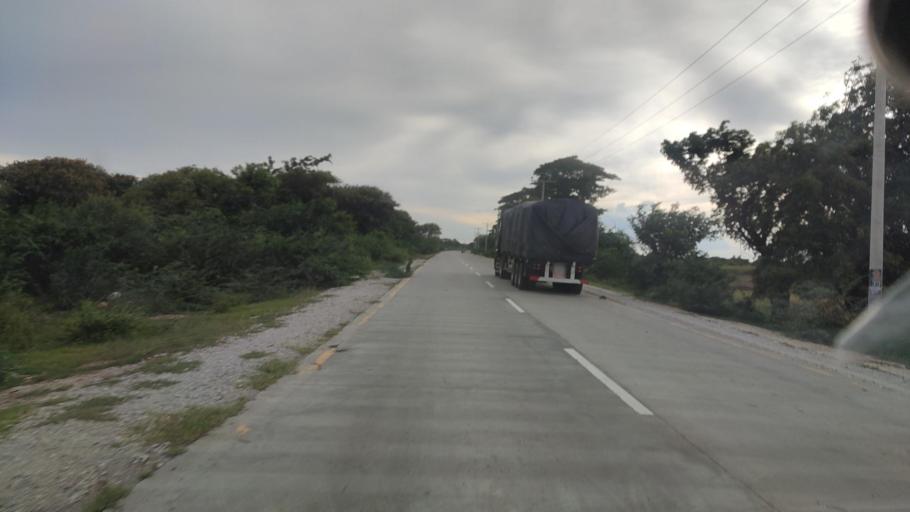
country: MM
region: Mandalay
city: Kyaukse
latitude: 21.3279
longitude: 96.0354
